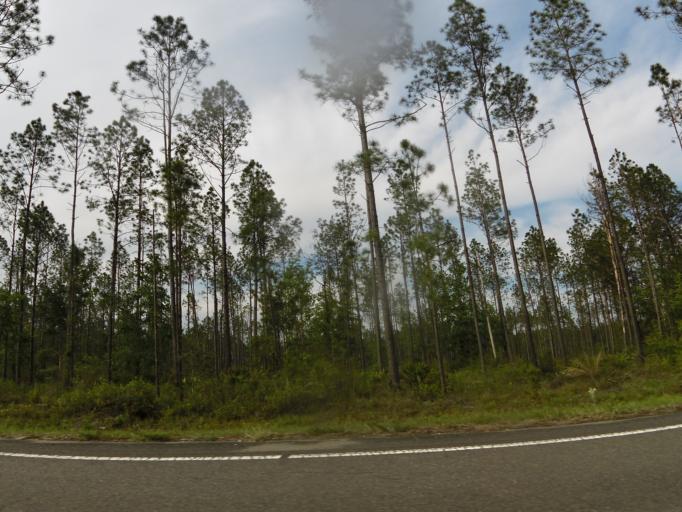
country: US
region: Florida
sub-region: Nassau County
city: Yulee
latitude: 30.6943
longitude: -81.6895
